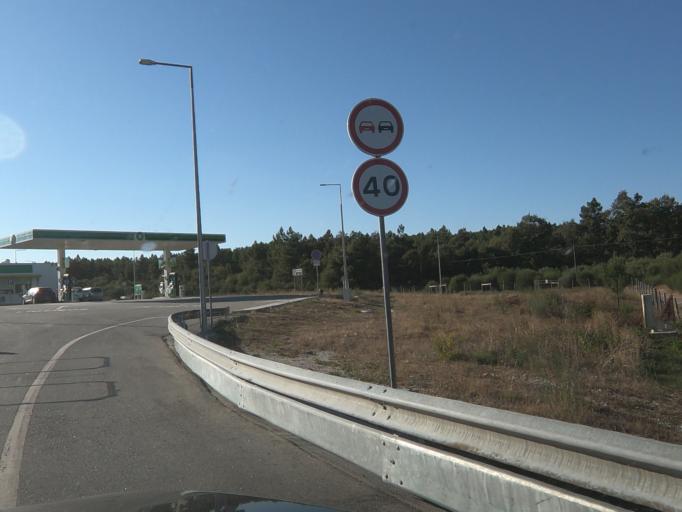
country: PT
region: Vila Real
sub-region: Sabrosa
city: Sabrosa
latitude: 41.3244
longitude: -7.6398
